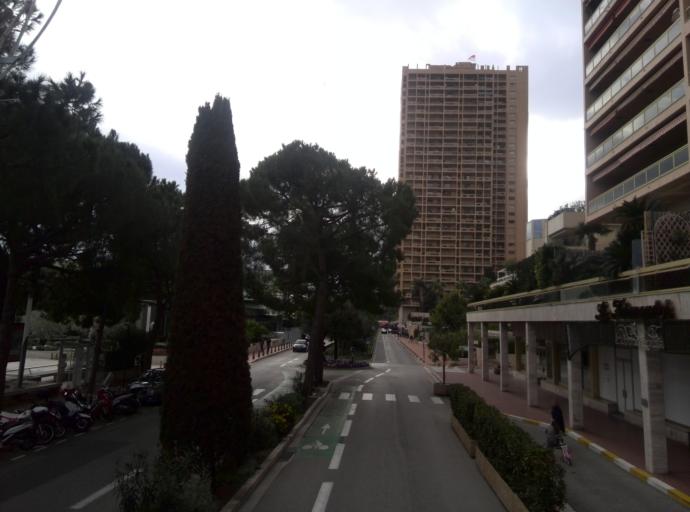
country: MC
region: Commune de Monaco
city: Saint-Roman
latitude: 43.7458
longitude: 7.4321
